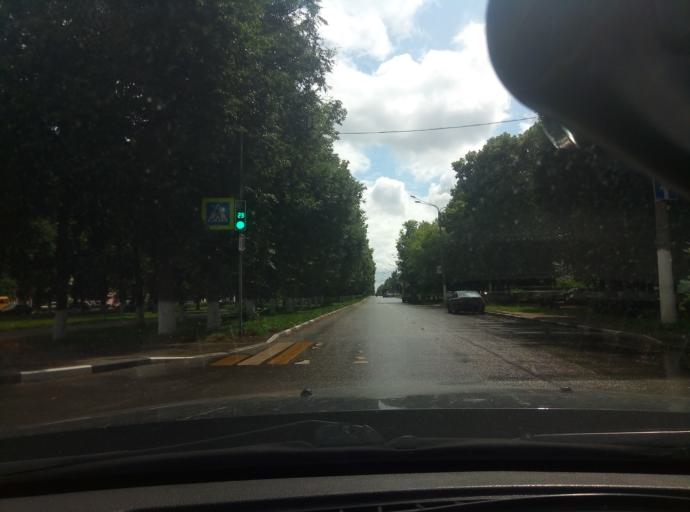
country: RU
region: Tula
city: Novomoskovsk
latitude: 54.0164
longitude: 38.2961
